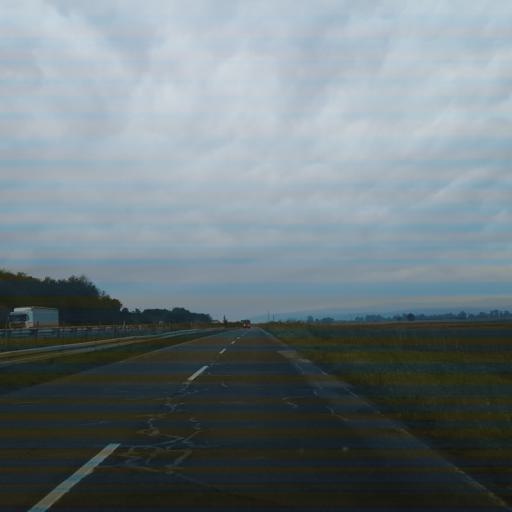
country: RS
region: Central Serbia
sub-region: Nisavski Okrug
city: Aleksinac
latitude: 43.5643
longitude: 21.6786
